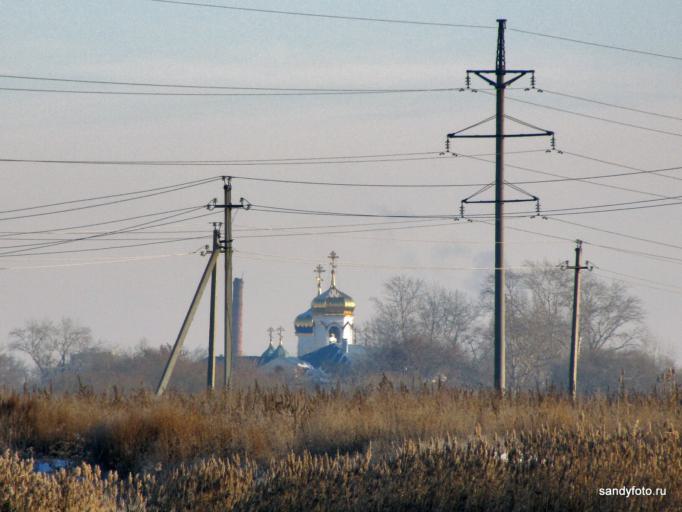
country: RU
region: Chelyabinsk
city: Troitsk
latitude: 54.0944
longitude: 61.5394
